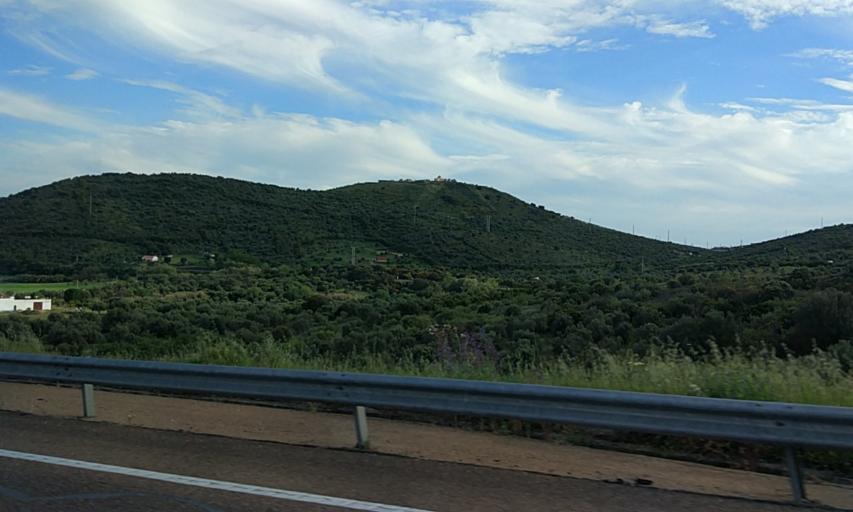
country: PT
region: Portalegre
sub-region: Elvas
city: Elvas
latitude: 38.9080
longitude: -7.1666
